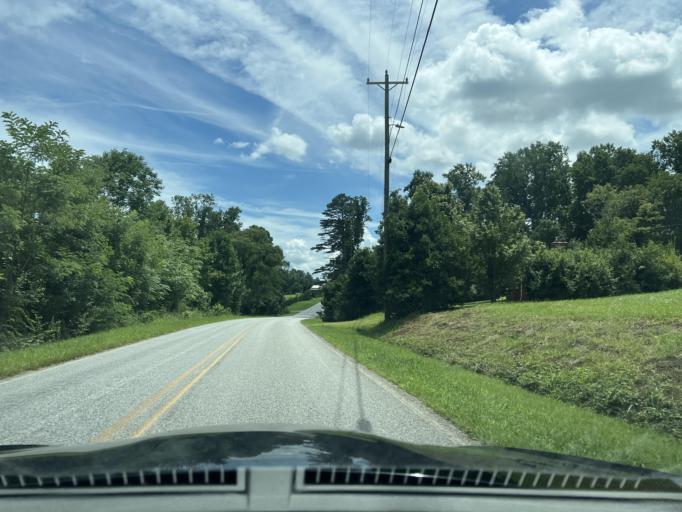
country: US
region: North Carolina
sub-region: Henderson County
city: Fruitland
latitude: 35.4026
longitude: -82.3912
